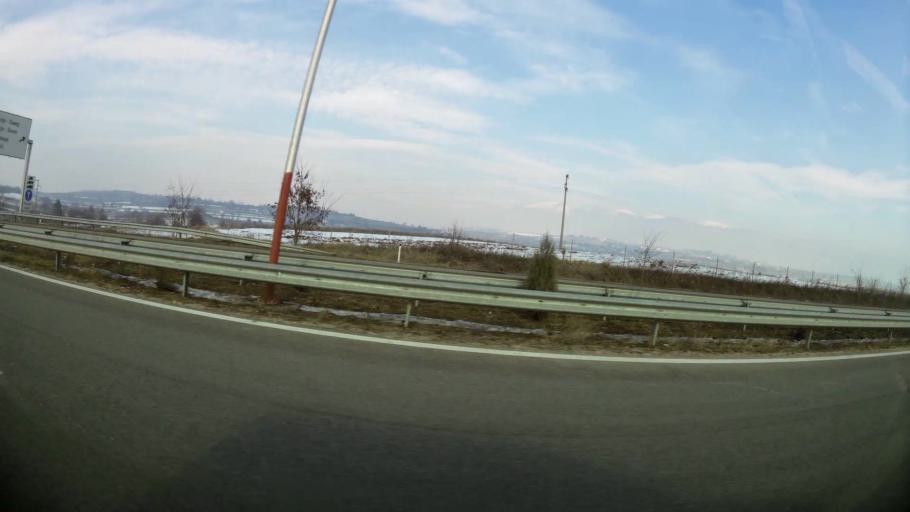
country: MK
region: Suto Orizari
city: Suto Orizare
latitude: 42.0515
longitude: 21.4274
